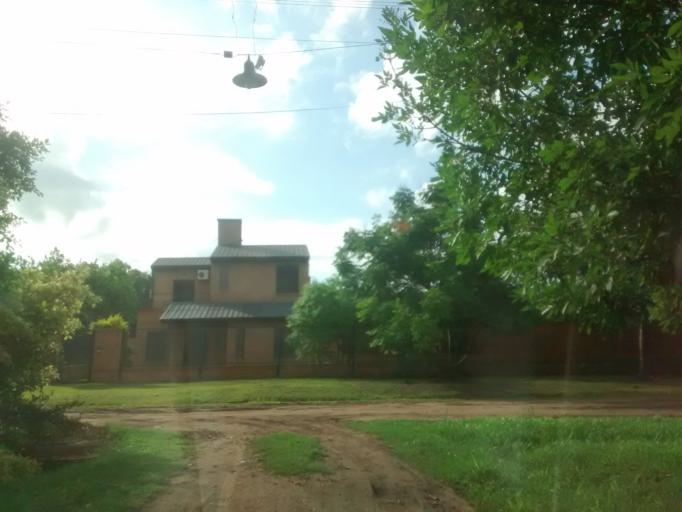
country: AR
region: Chaco
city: Puerto Tirol
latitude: -27.3770
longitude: -59.0880
